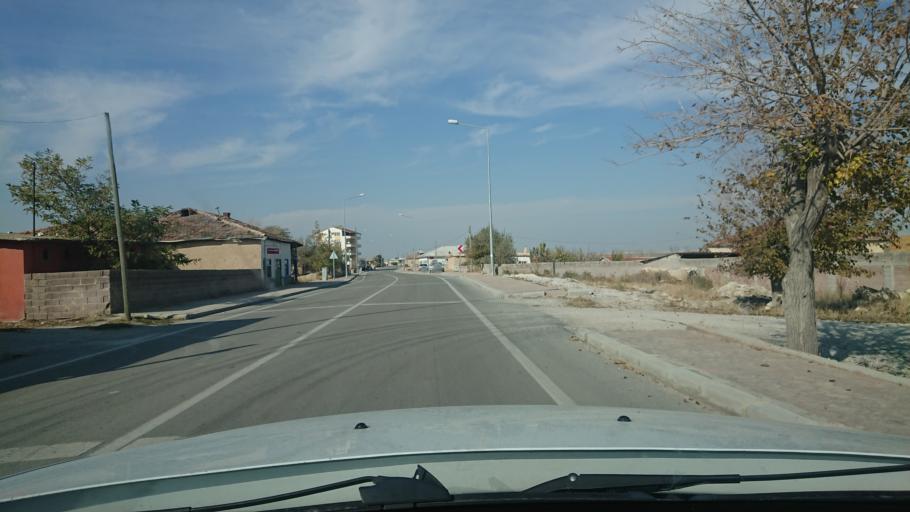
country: TR
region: Aksaray
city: Sultanhani
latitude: 38.2615
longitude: 33.4442
